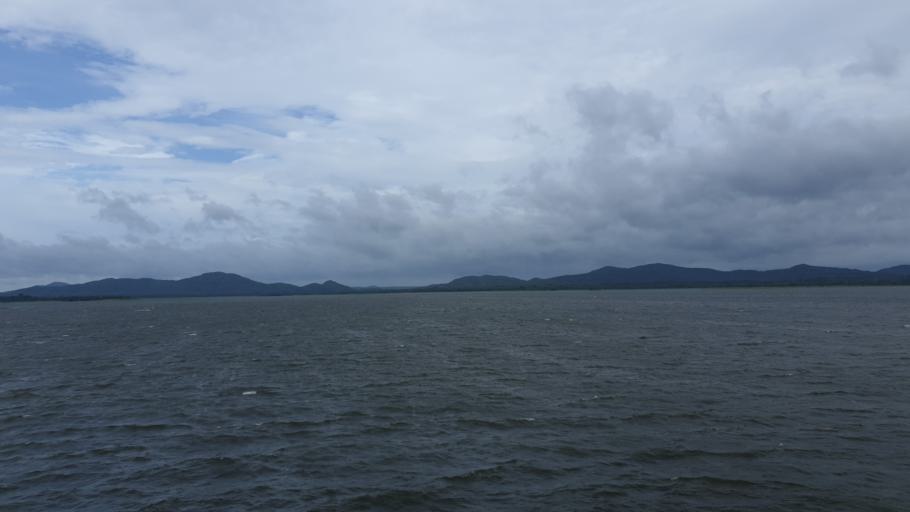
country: LK
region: North Central
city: Polonnaruwa
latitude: 8.0328
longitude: 80.8950
